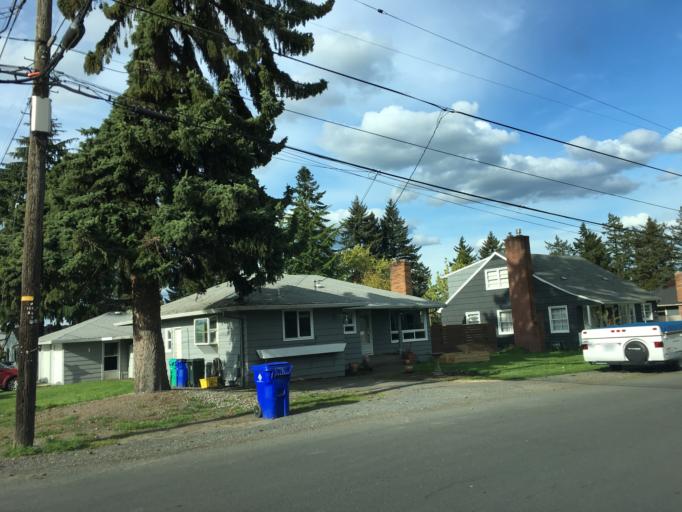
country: US
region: Oregon
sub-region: Multnomah County
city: Lents
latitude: 45.5456
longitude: -122.5515
